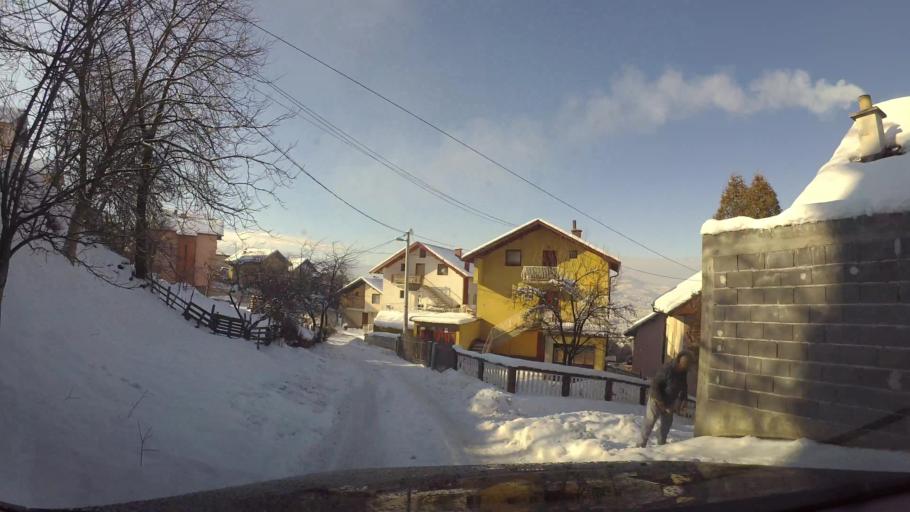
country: BA
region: Federation of Bosnia and Herzegovina
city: Kobilja Glava
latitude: 43.8789
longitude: 18.4236
